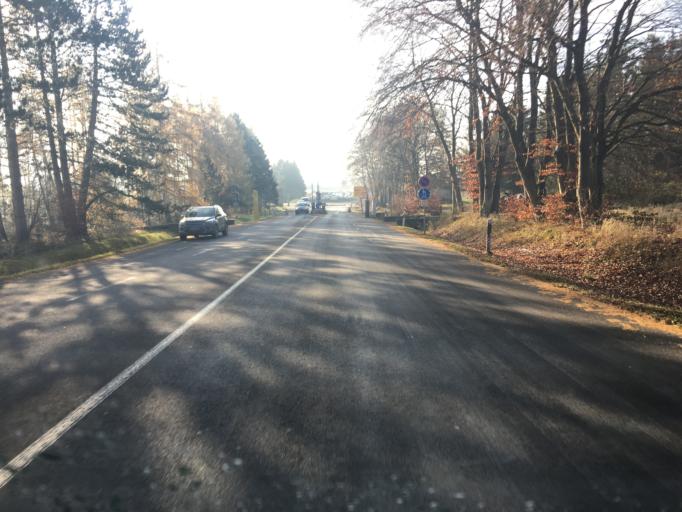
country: DE
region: North Rhine-Westphalia
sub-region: Regierungsbezirk Koln
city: Schleiden
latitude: 50.5694
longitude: 6.4384
